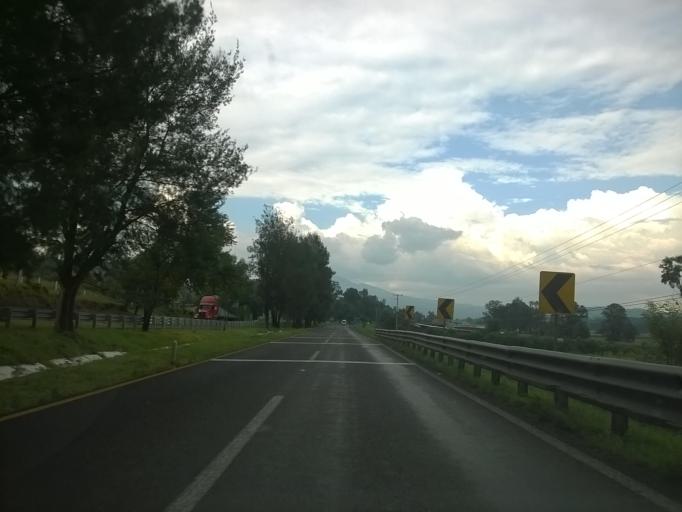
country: MX
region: Michoacan
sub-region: Huiramba
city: El Pedregal
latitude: 19.5319
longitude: -101.4760
